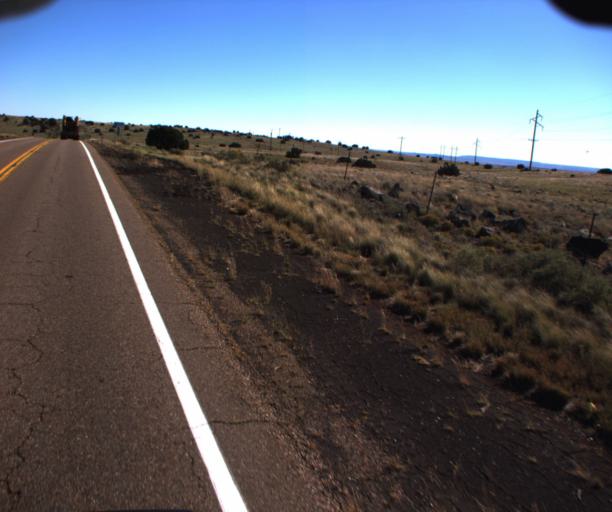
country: US
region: Arizona
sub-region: Apache County
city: Saint Johns
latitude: 34.4946
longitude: -109.5112
